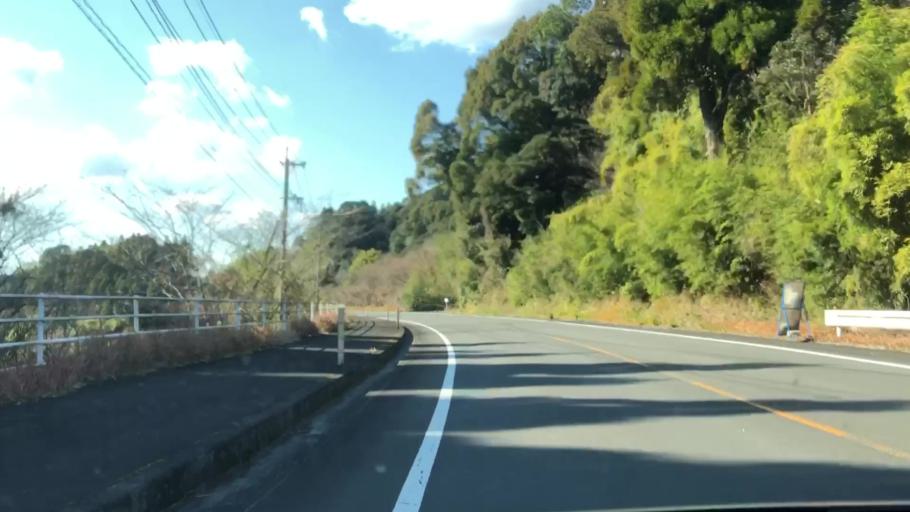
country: JP
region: Kagoshima
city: Satsumasendai
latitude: 31.8625
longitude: 130.4005
